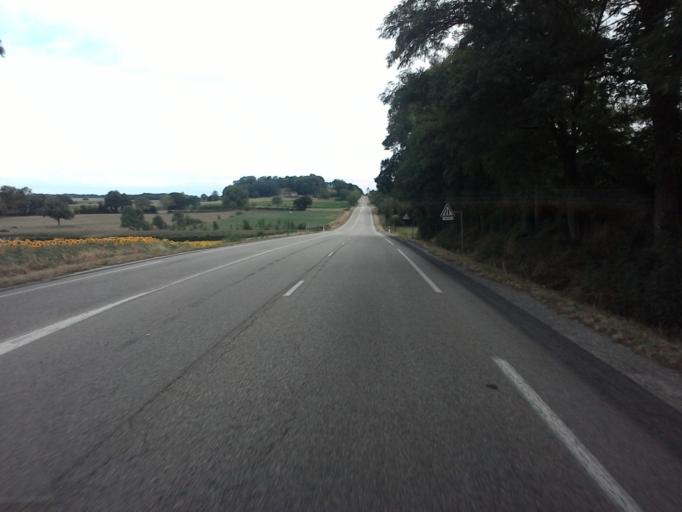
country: FR
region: Rhone-Alpes
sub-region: Departement de l'Ain
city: Saint-Martin-du-Mont
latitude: 46.0740
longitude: 5.3234
